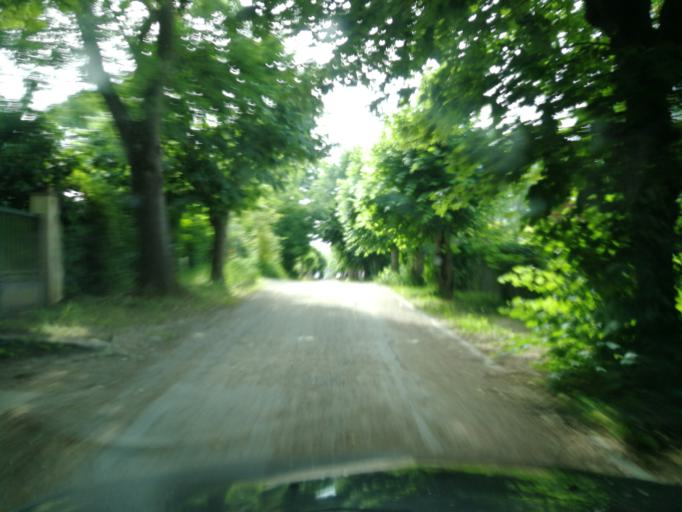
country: FR
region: Ile-de-France
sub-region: Departement des Yvelines
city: Saint-Remy-les-Chevreuse
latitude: 48.7014
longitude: 2.0774
